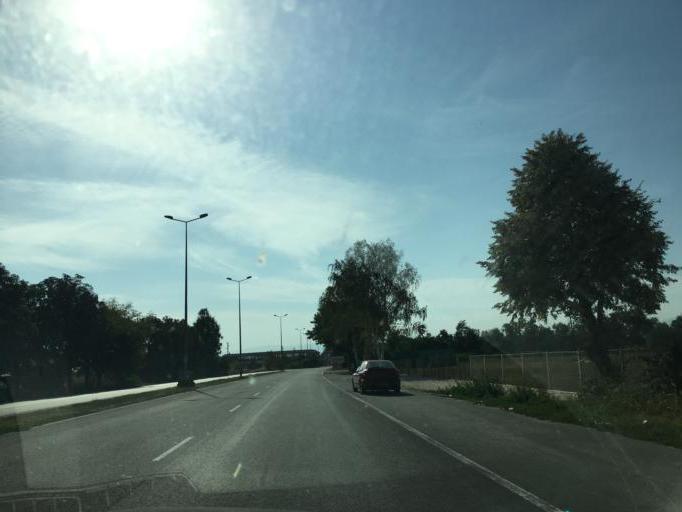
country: BG
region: Pazardzhik
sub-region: Obshtina Pazardzhik
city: Pazardzhik
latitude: 42.2138
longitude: 24.3210
